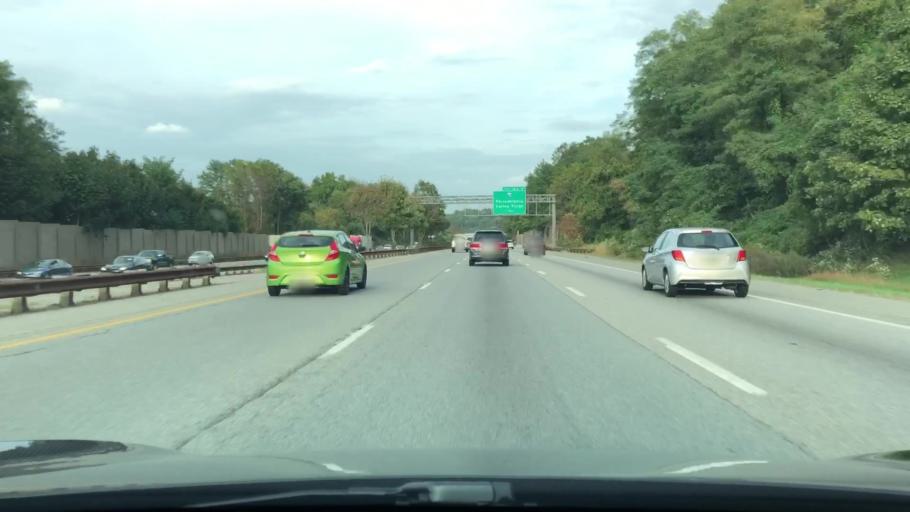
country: US
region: Pennsylvania
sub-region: Delaware County
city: Radnor
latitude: 40.0535
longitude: -75.3403
